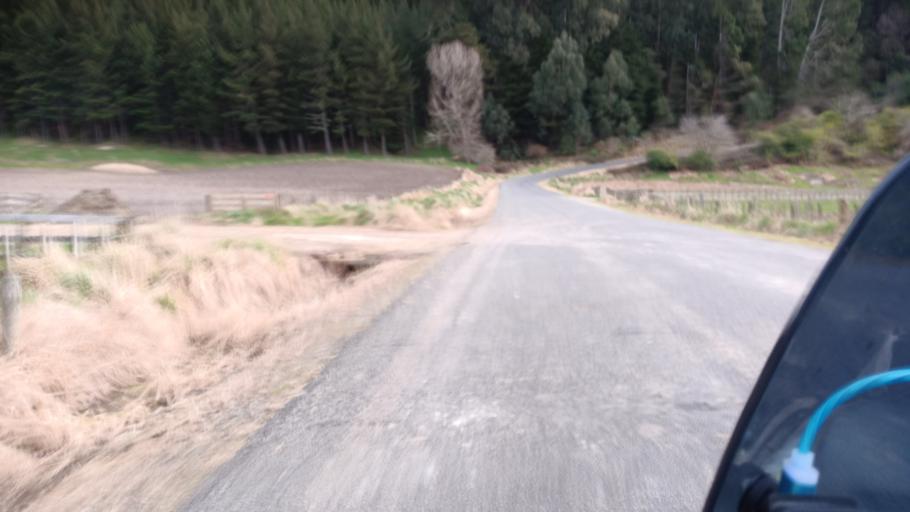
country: NZ
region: Hawke's Bay
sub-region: Wairoa District
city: Wairoa
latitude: -38.8182
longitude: 177.4731
